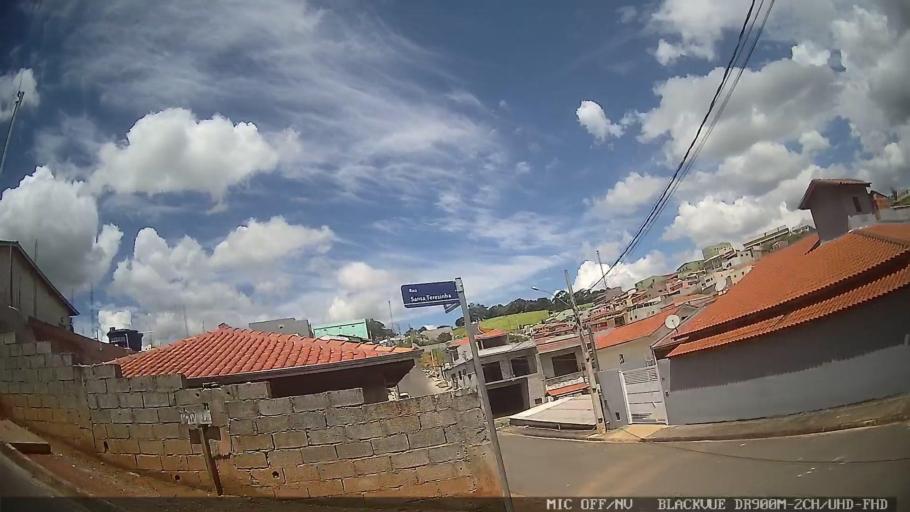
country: BR
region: Minas Gerais
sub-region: Extrema
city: Extrema
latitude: -22.7385
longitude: -46.3803
